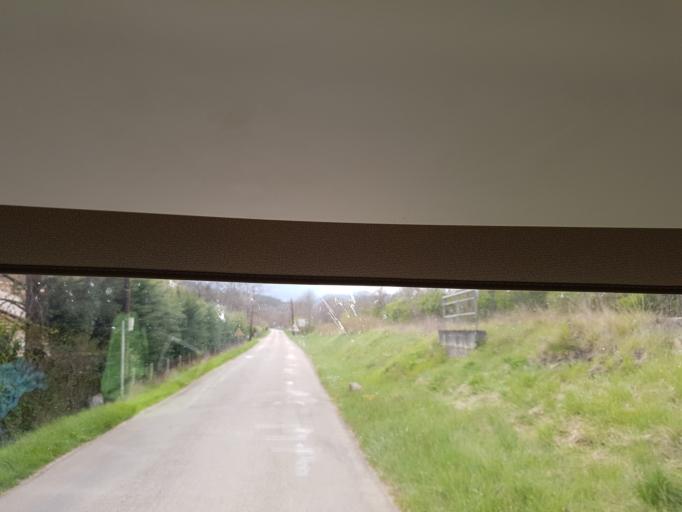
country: FR
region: Languedoc-Roussillon
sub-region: Departement de l'Aude
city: Quillan
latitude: 42.9085
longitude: 2.1917
